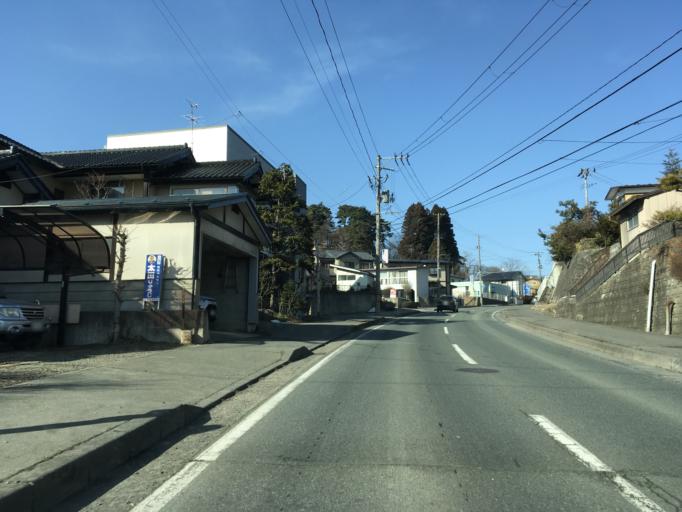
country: JP
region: Iwate
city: Morioka-shi
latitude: 39.7186
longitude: 141.1546
